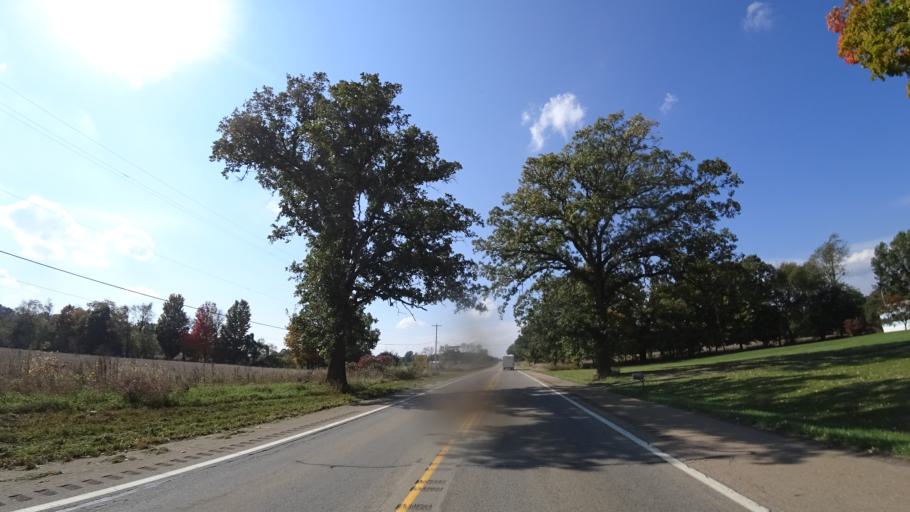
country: US
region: Michigan
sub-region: Jackson County
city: Concord
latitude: 42.1626
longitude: -84.7204
